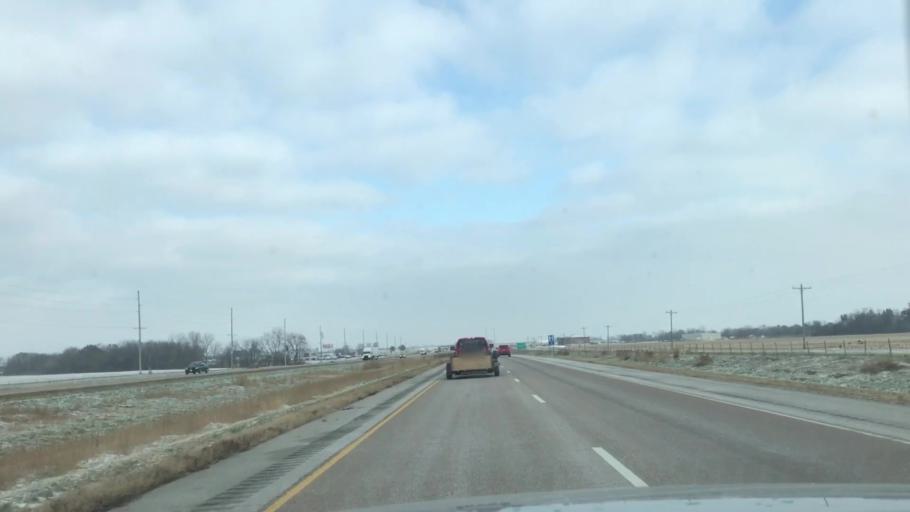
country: US
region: Illinois
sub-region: Macoupin County
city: Staunton
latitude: 39.0066
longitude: -89.7494
